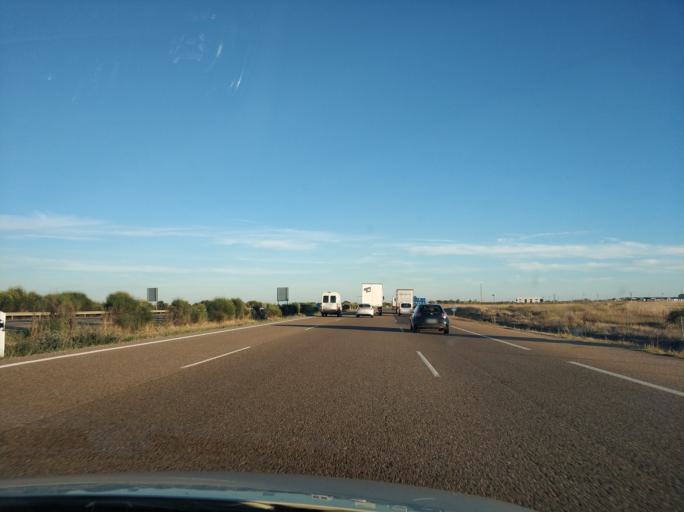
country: ES
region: Castille and Leon
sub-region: Provincia de Zamora
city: San Cristobal de Entrevinas
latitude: 42.0474
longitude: -5.6747
